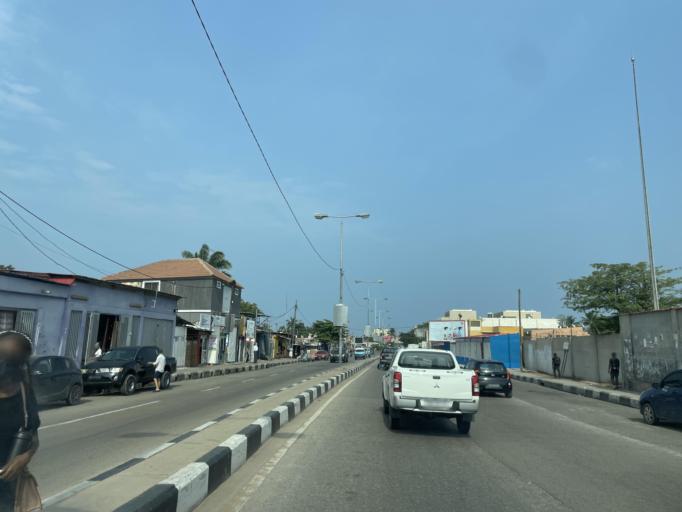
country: AO
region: Luanda
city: Luanda
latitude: -8.8306
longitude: 13.2197
